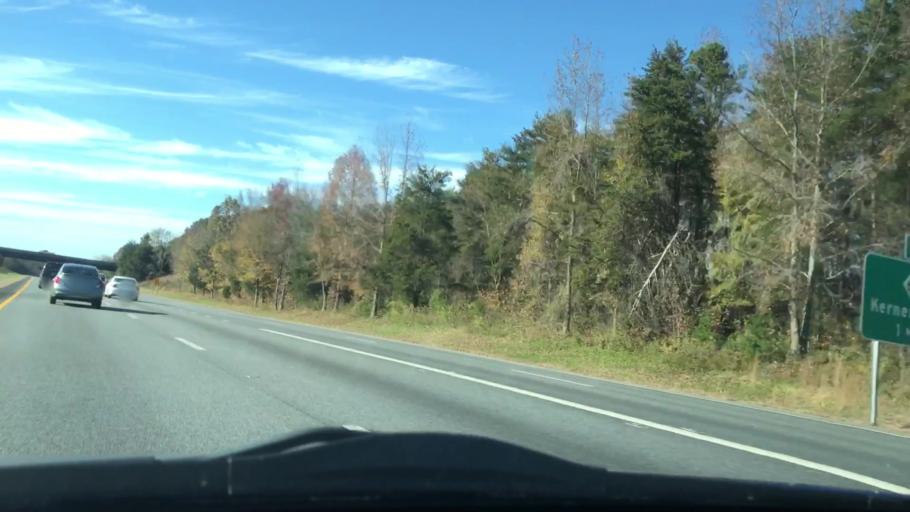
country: US
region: North Carolina
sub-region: Guilford County
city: High Point
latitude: 36.0158
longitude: -80.0400
